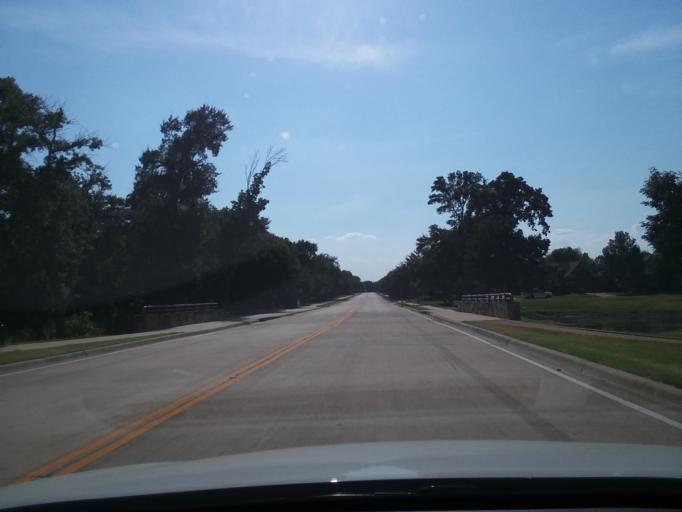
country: US
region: Texas
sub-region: Denton County
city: Double Oak
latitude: 33.0475
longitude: -97.0789
